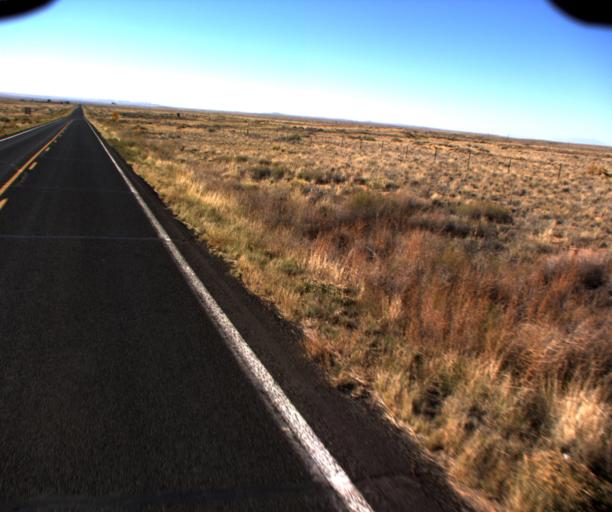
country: US
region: Arizona
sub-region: Navajo County
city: First Mesa
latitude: 35.7882
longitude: -110.4983
